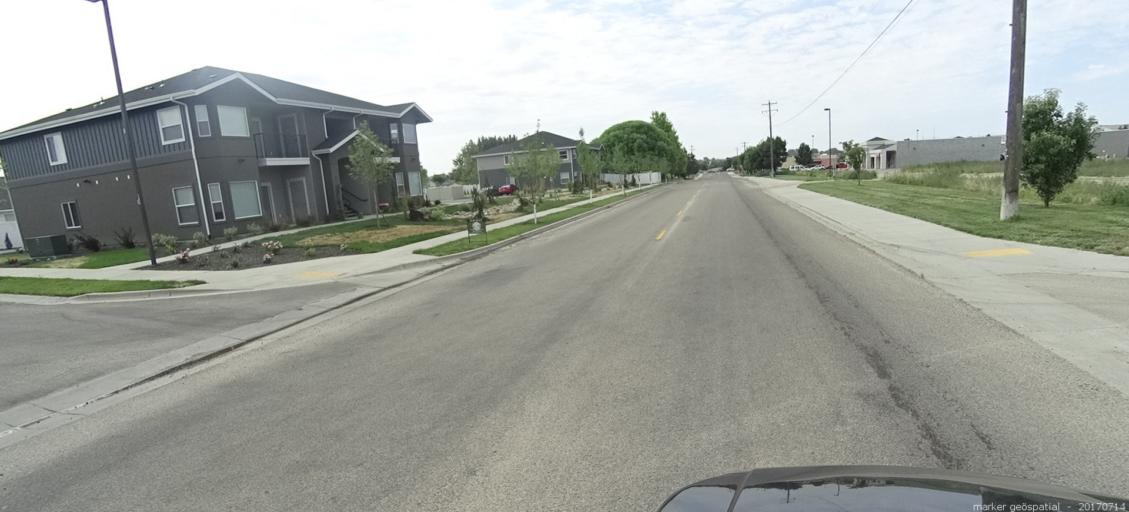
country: US
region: Idaho
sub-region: Ada County
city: Kuna
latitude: 43.4911
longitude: -116.4039
